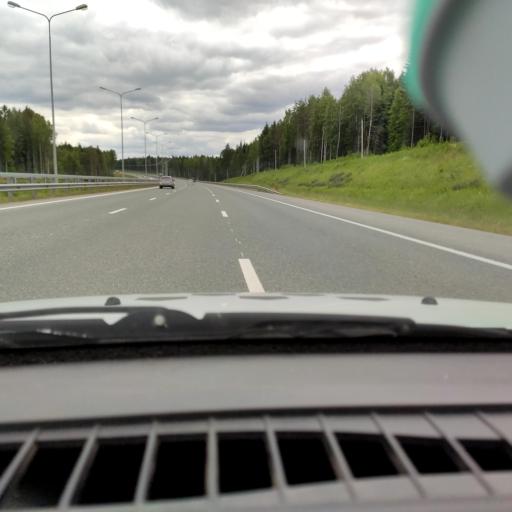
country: RU
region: Perm
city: Zvezdnyy
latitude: 57.7521
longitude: 56.3331
